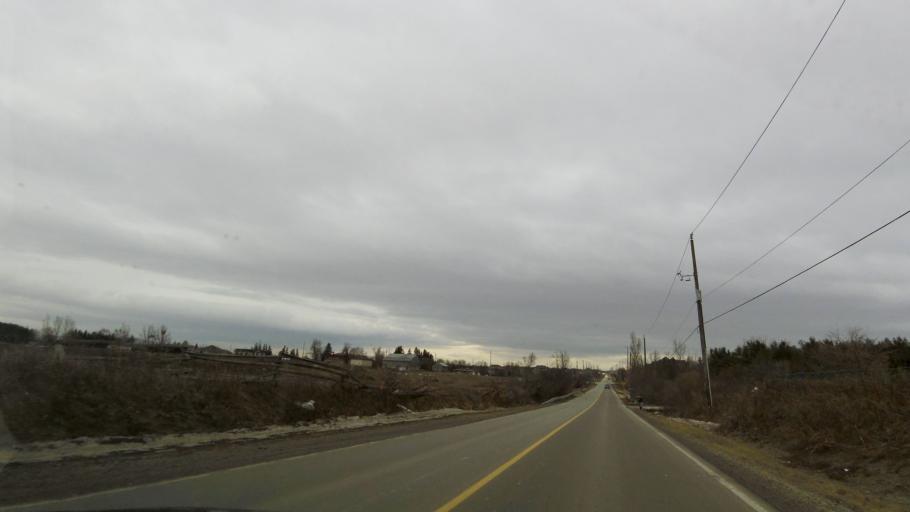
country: CA
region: Ontario
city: Brampton
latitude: 43.8140
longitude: -79.7141
